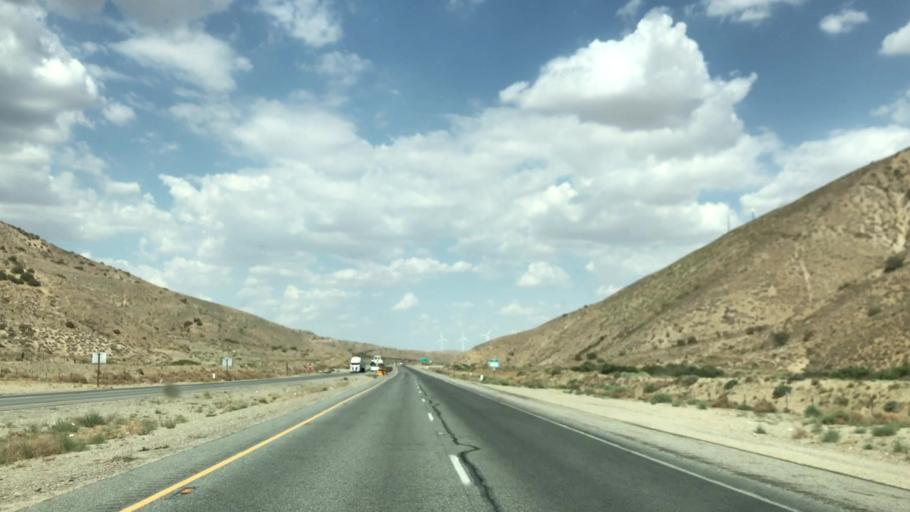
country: US
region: California
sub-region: Kern County
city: Mojave
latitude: 35.1008
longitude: -118.2867
